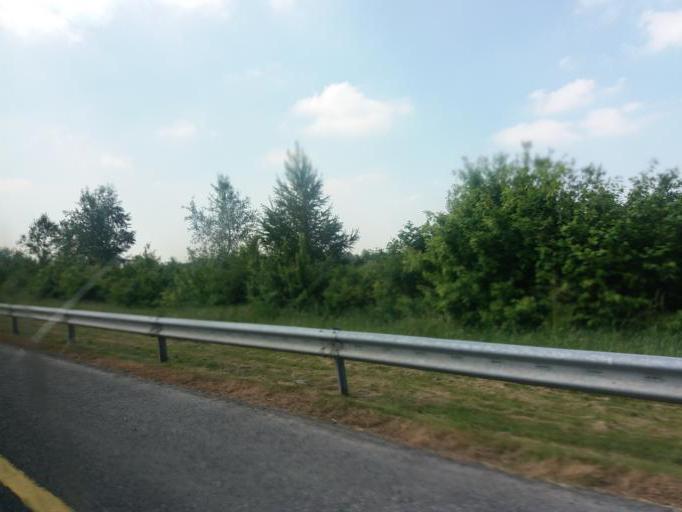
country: IE
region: Leinster
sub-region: An Mhi
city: Ashbourne
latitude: 53.5052
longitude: -6.4195
